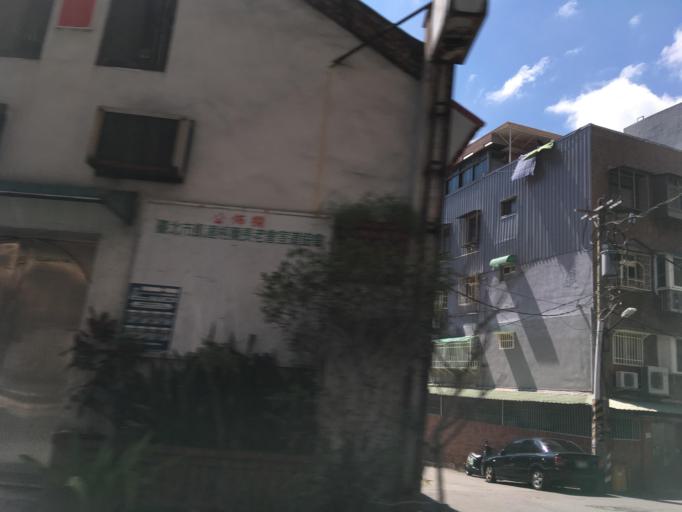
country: TW
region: Taipei
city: Taipei
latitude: 25.1424
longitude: 121.4986
